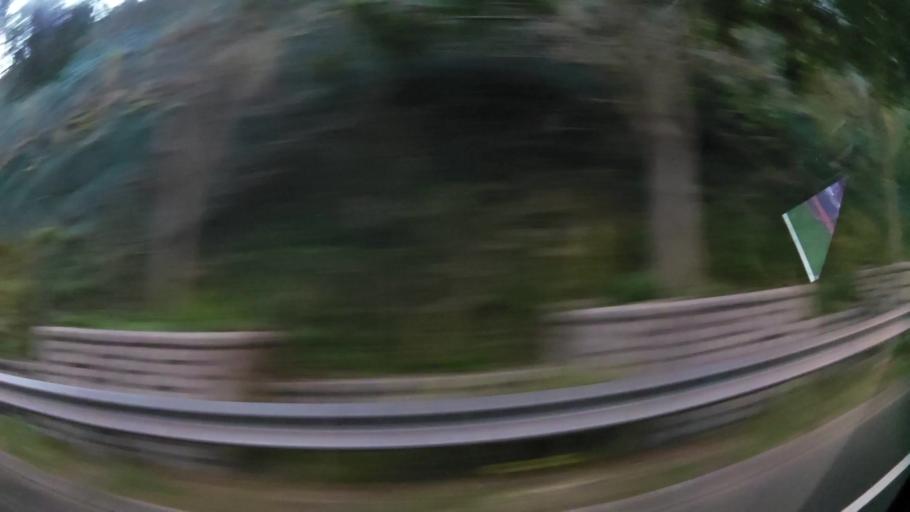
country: HK
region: Tsuen Wan
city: Tsuen Wan
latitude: 22.3603
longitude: 114.0981
